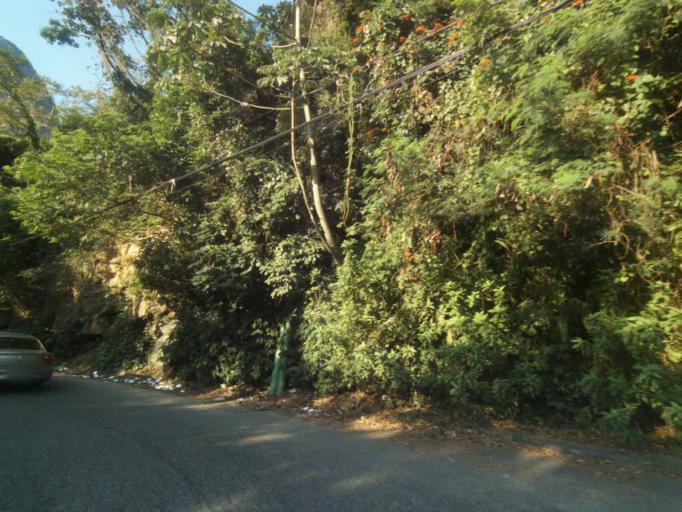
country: BR
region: Rio de Janeiro
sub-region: Rio De Janeiro
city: Rio de Janeiro
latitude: -23.0094
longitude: -43.2905
